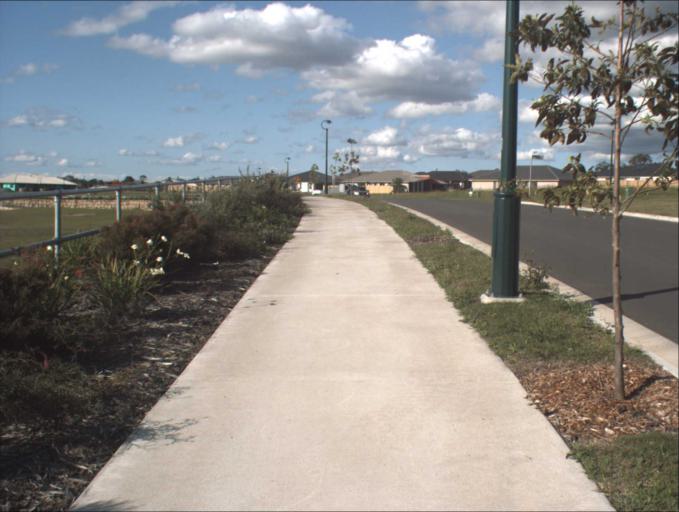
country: AU
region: Queensland
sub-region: Logan
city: Chambers Flat
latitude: -27.7770
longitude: 153.0974
